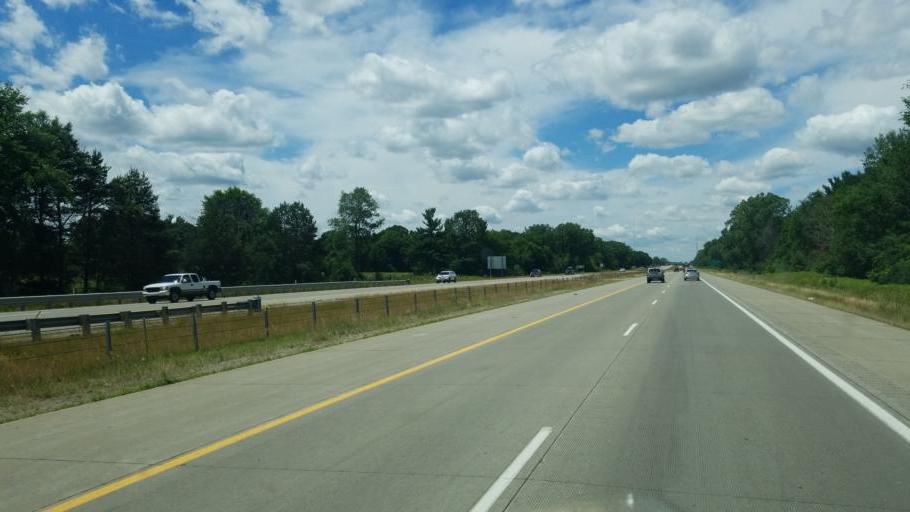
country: US
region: Michigan
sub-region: Ingham County
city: Okemos
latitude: 42.6781
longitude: -84.4629
